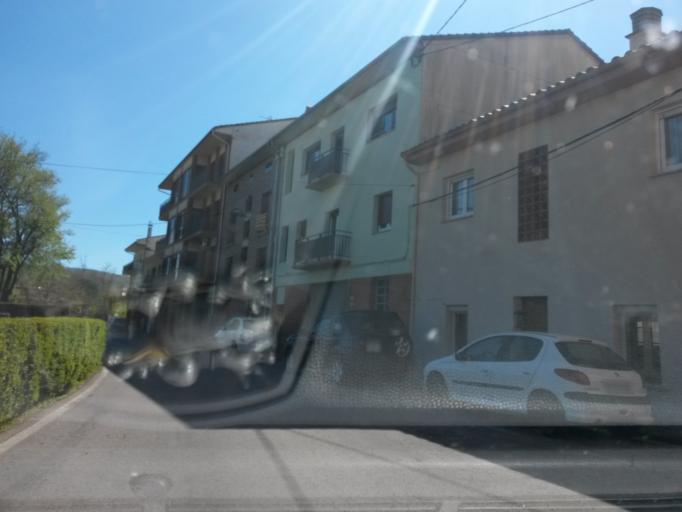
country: ES
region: Catalonia
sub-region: Provincia de Girona
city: Olot
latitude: 42.1691
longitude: 2.4791
